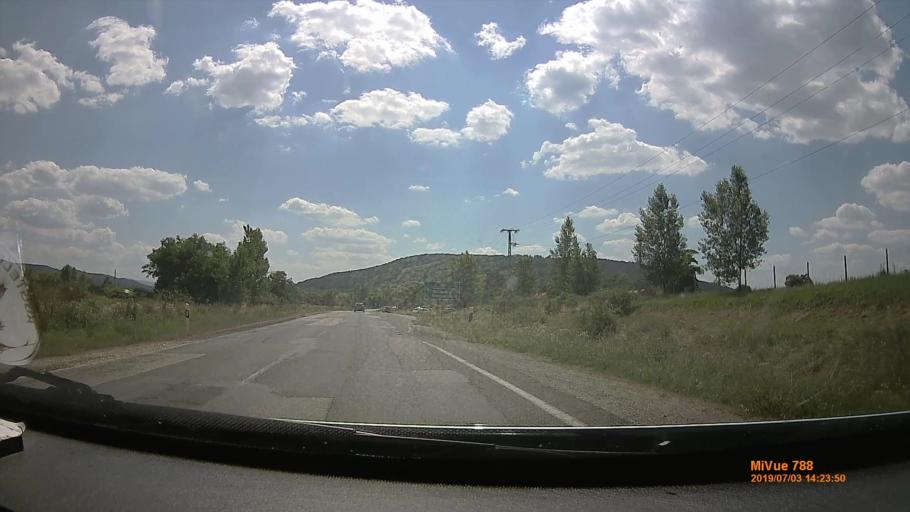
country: HU
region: Borsod-Abauj-Zemplen
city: Sajokaza
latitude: 48.2727
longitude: 20.5486
